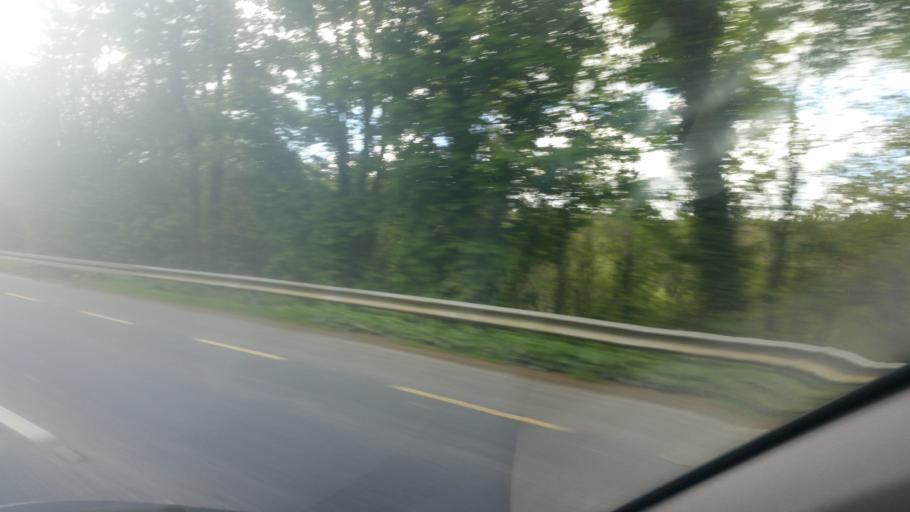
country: IE
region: Leinster
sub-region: Loch Garman
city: Enniscorthy
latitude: 52.4831
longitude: -6.5648
